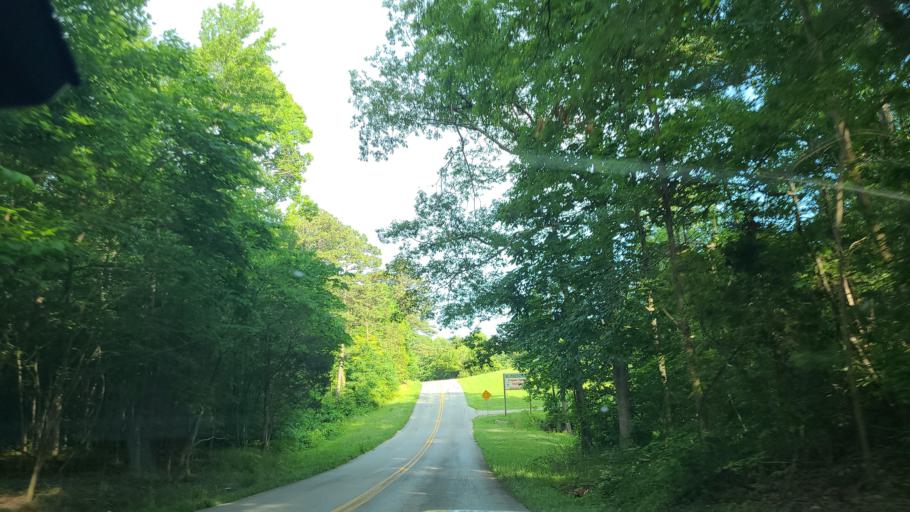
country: US
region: Kentucky
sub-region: Whitley County
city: Corbin
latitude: 36.8842
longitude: -84.2116
